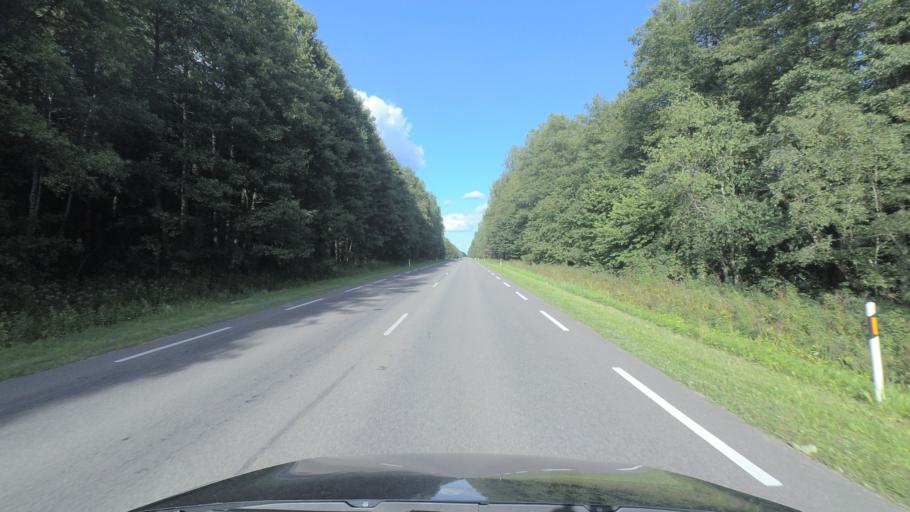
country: LT
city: Pabrade
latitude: 54.9652
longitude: 25.7101
